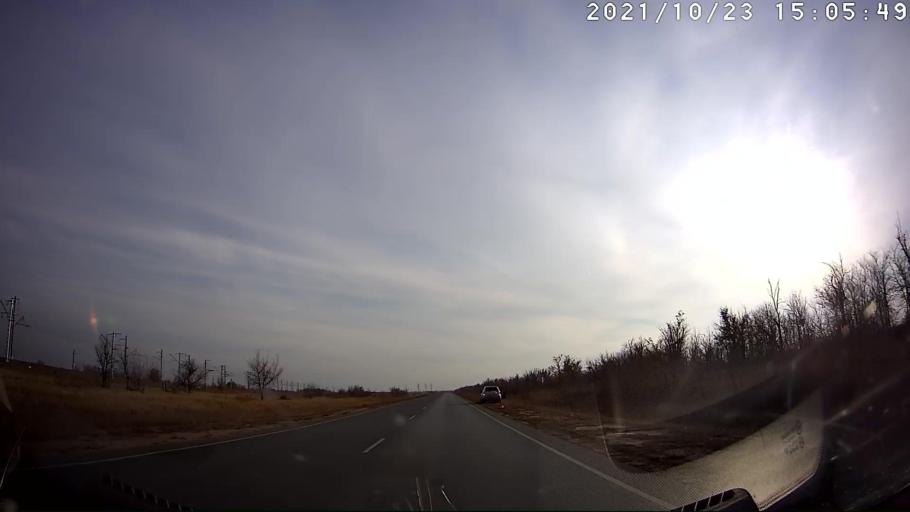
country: RU
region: Volgograd
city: Volgograd
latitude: 48.3793
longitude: 44.3590
